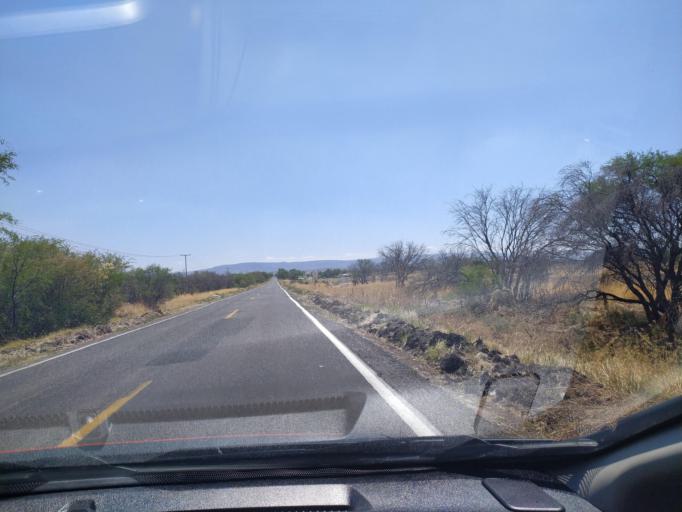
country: MX
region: Guanajuato
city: Ciudad Manuel Doblado
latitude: 20.7754
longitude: -101.8320
